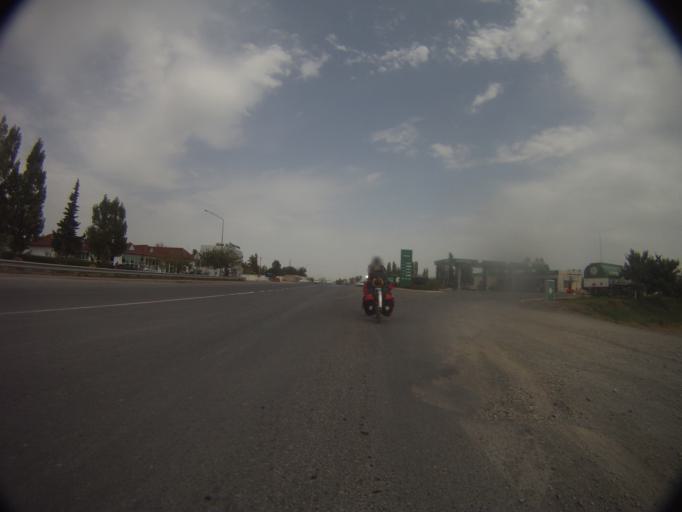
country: AZ
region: Ucar
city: Ujar
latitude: 40.4952
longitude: 47.6673
